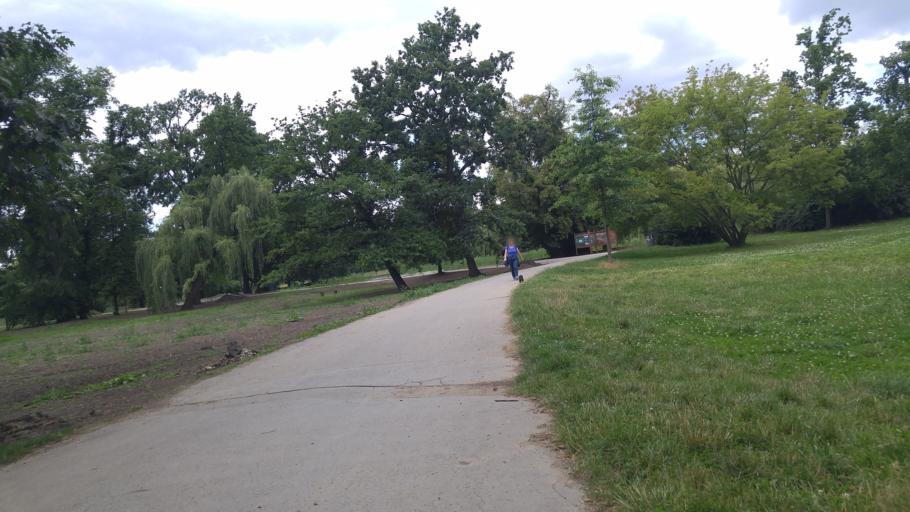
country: CZ
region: Praha
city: Prague
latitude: 50.1063
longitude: 14.4226
